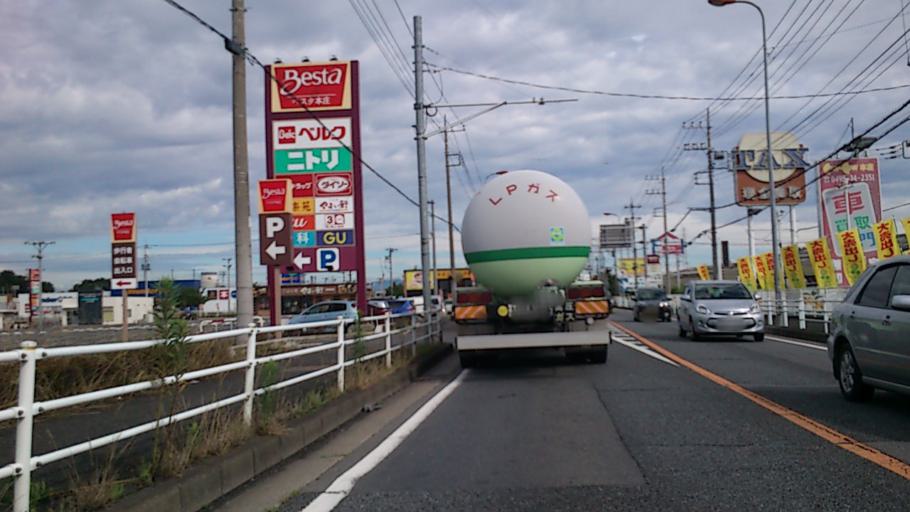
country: JP
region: Saitama
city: Honjo
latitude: 36.2324
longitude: 139.2114
